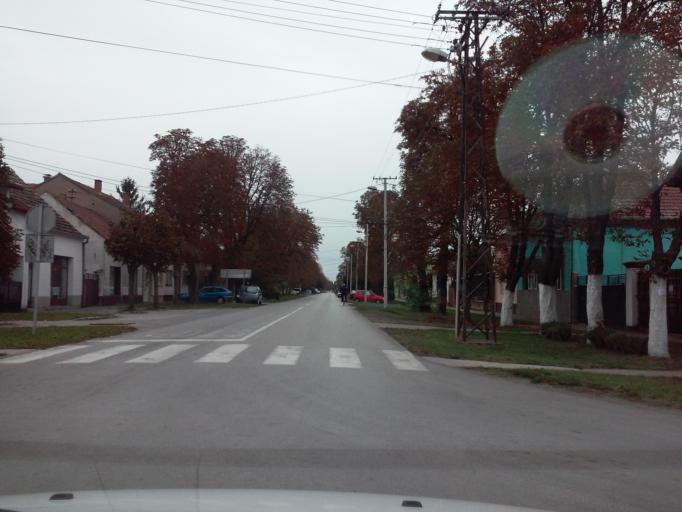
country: RS
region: Autonomna Pokrajina Vojvodina
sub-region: Severnobanatski Okrug
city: Kikinda
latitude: 45.8227
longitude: 20.4738
